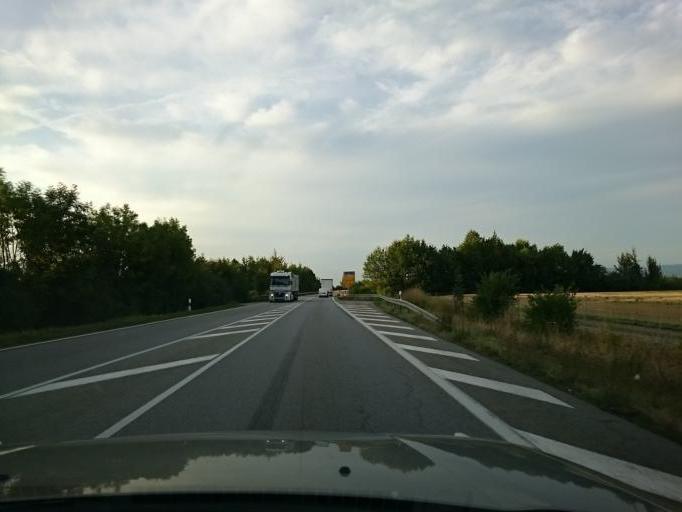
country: DE
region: Bavaria
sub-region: Lower Bavaria
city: Oberschneiding
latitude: 48.7843
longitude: 12.6501
